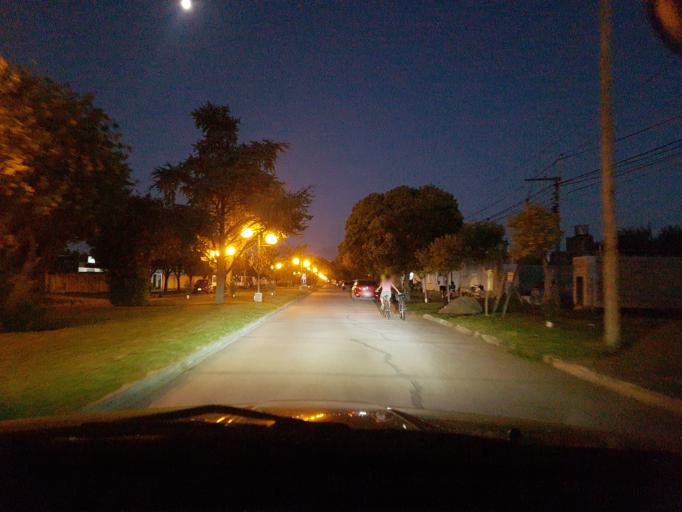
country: AR
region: Cordoba
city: Las Perdices
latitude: -32.7570
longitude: -63.7825
